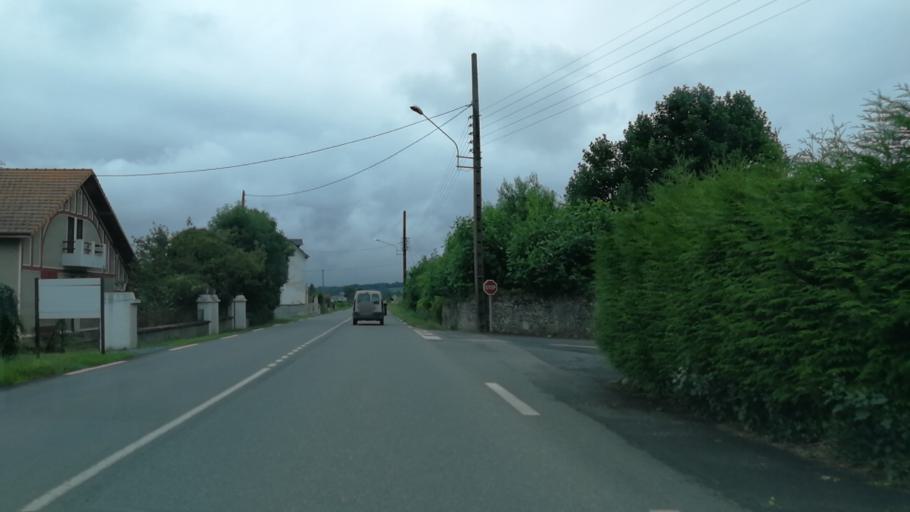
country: FR
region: Aquitaine
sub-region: Departement des Pyrenees-Atlantiques
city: Oloron-Sainte-Marie
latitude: 43.1468
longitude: -0.6007
